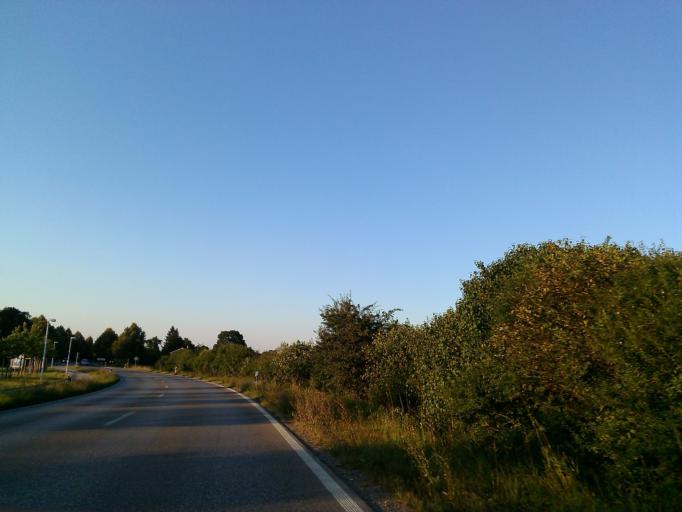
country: DE
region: Bavaria
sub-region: Upper Bavaria
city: Krailling
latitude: 48.0806
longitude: 11.3981
